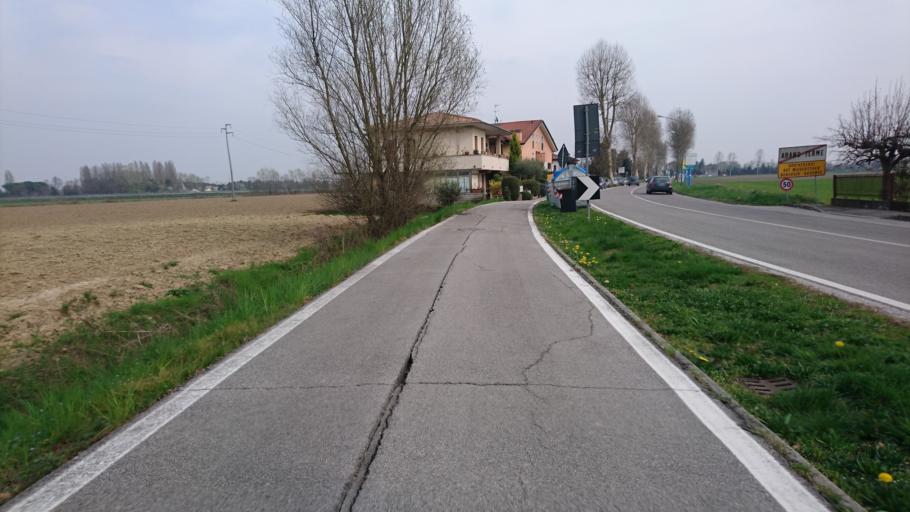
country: IT
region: Veneto
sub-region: Provincia di Padova
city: Abano Terme
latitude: 45.3613
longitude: 11.8055
